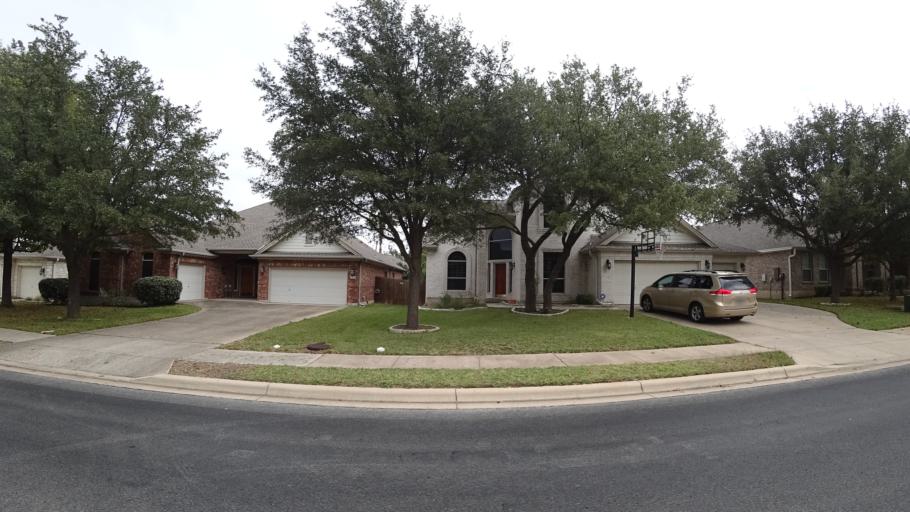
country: US
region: Texas
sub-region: Williamson County
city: Brushy Creek
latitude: 30.5140
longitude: -97.7480
